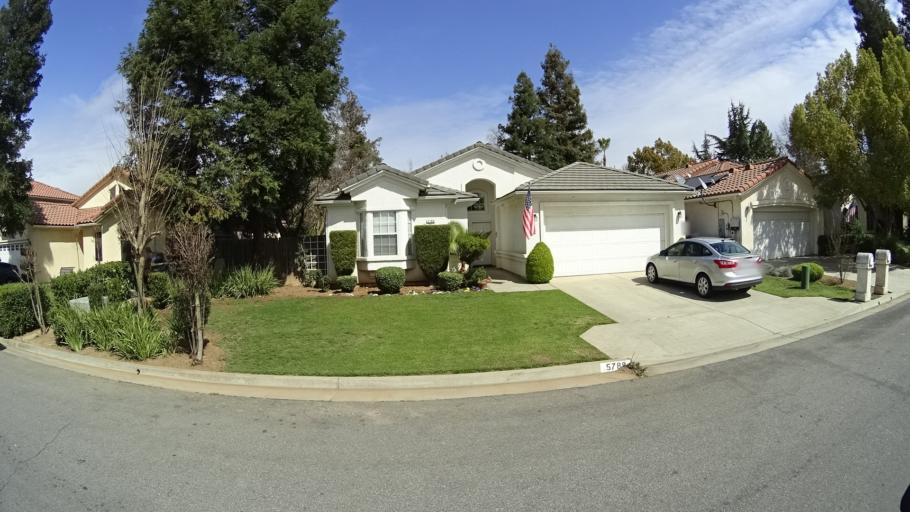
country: US
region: California
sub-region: Fresno County
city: Biola
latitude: 36.8464
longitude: -119.8951
